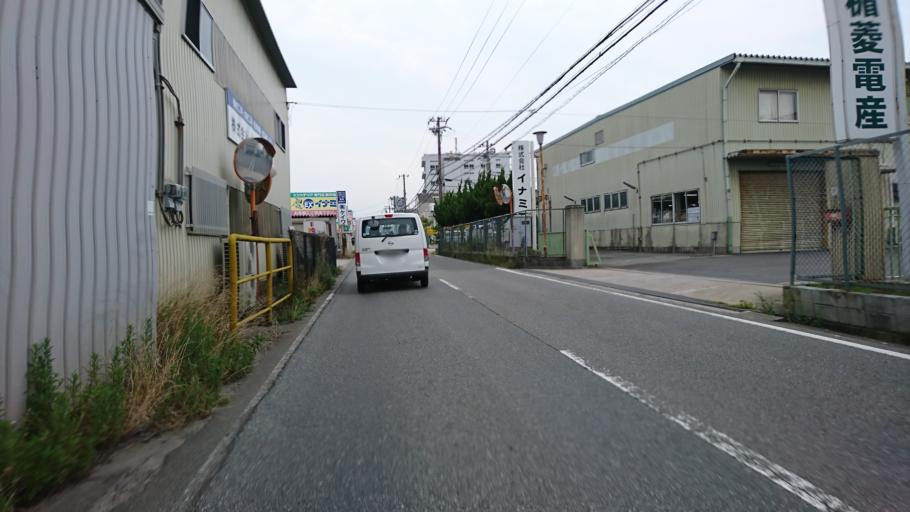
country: JP
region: Hyogo
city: Miki
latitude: 34.7308
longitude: 134.9190
